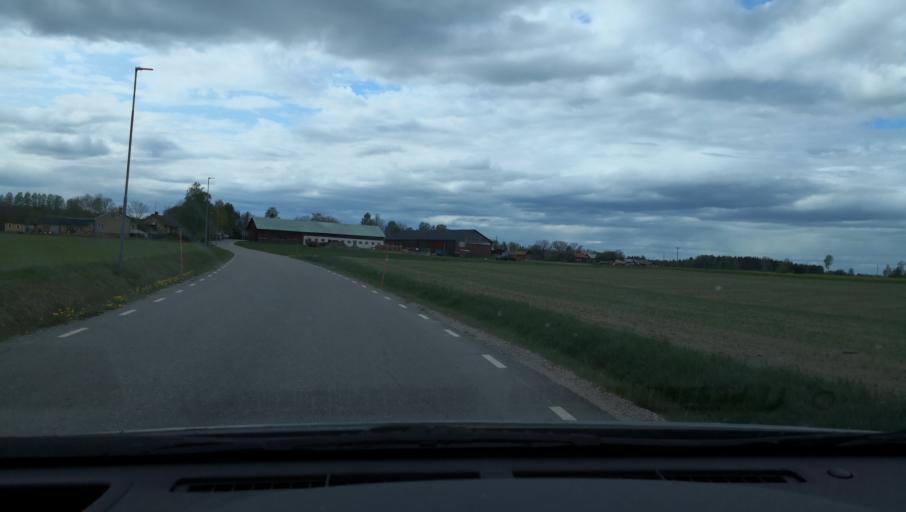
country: SE
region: Dalarna
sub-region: Avesta Kommun
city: Avesta
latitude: 60.0208
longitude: 16.2771
